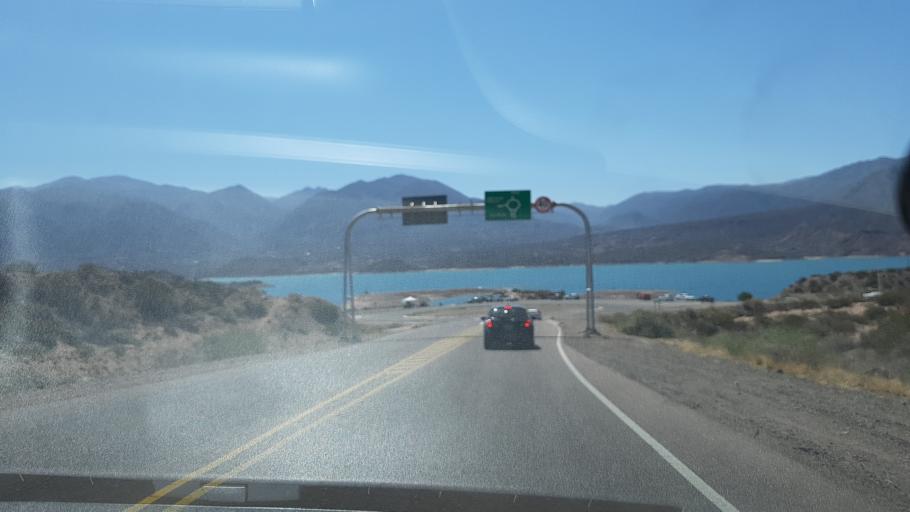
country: AR
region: Mendoza
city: Lujan de Cuyo
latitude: -32.9901
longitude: -69.1668
